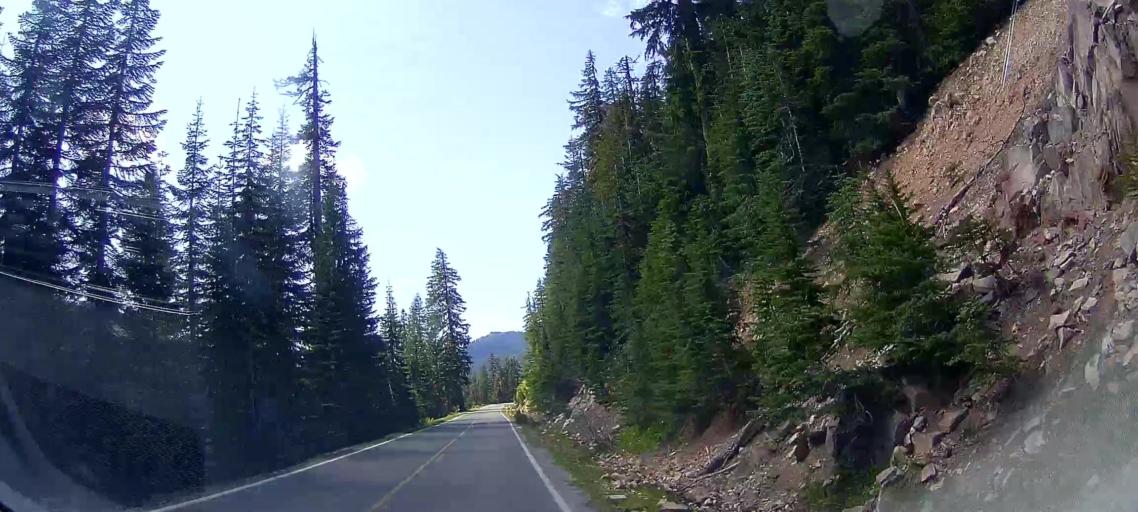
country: US
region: Oregon
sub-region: Klamath County
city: Klamath Falls
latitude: 42.8893
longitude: -122.0961
